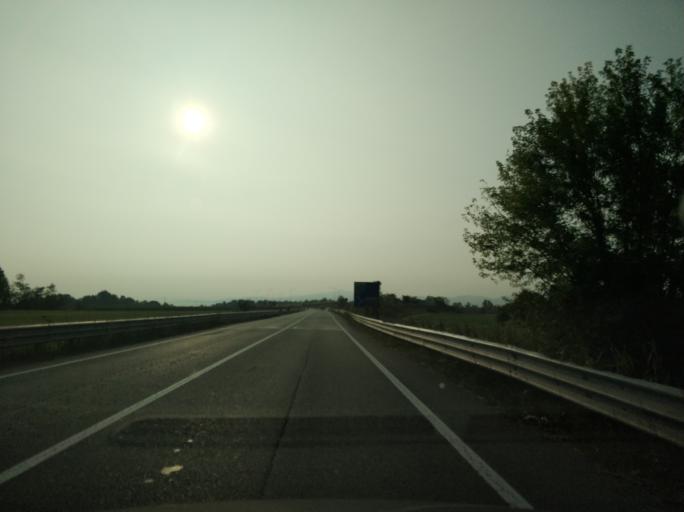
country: IT
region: Piedmont
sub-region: Provincia di Torino
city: Venaria Reale
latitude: 45.1530
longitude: 7.6190
